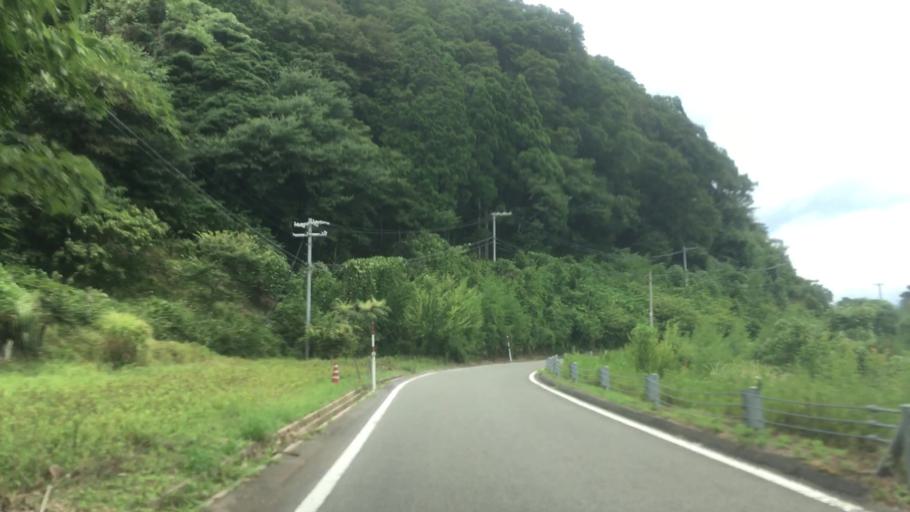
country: JP
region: Hyogo
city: Toyooka
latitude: 35.5831
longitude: 134.7988
